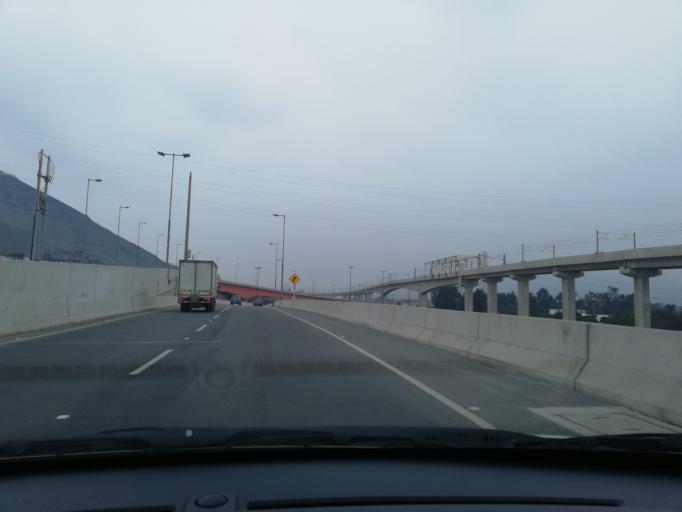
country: PE
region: Lima
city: Lima
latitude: -12.0399
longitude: -77.0139
